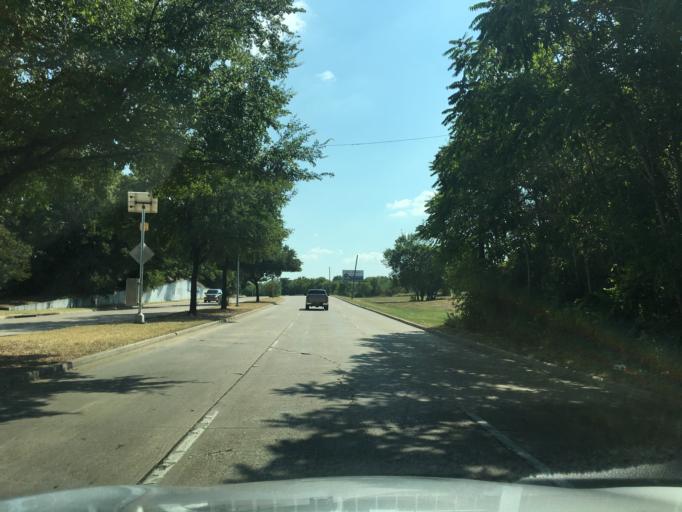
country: US
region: Texas
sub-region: Dallas County
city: Dallas
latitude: 32.7347
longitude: -96.7998
